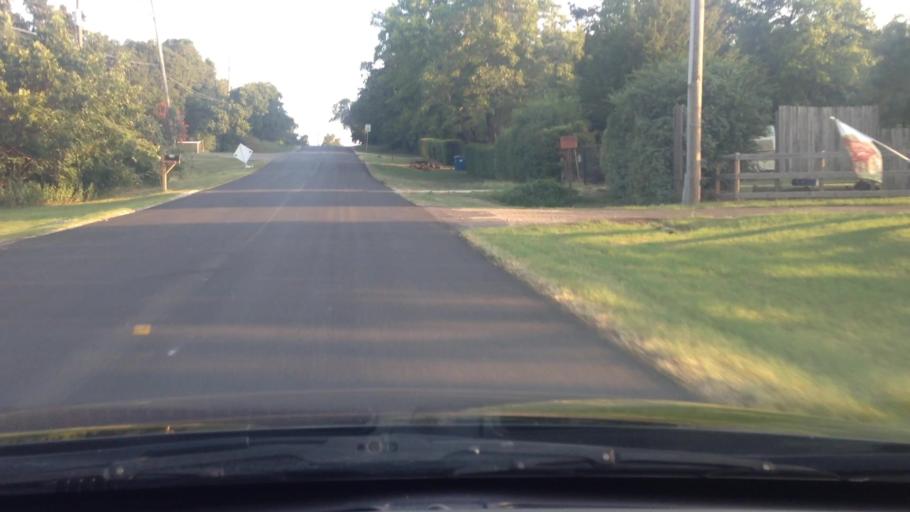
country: US
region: Texas
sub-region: Tarrant County
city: Rendon
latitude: 32.5972
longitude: -97.2502
